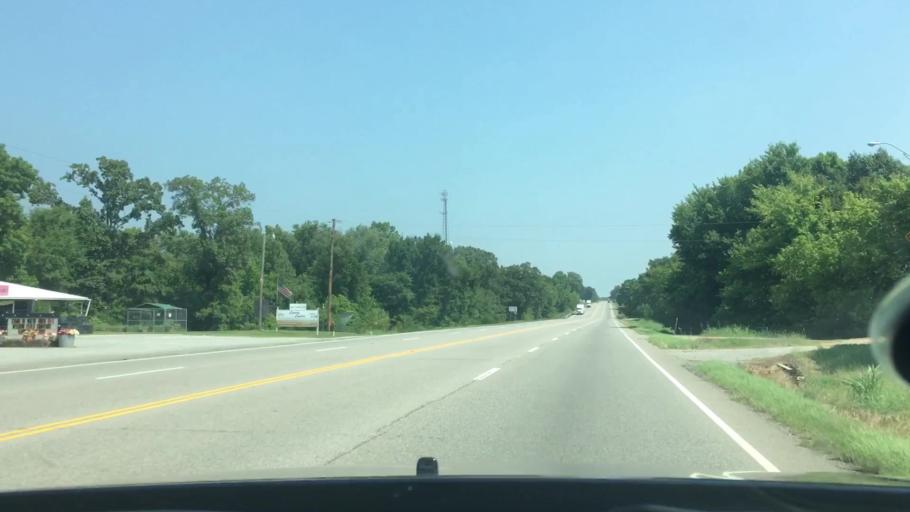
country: US
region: Oklahoma
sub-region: Atoka County
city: Atoka
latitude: 34.3264
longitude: -96.1638
